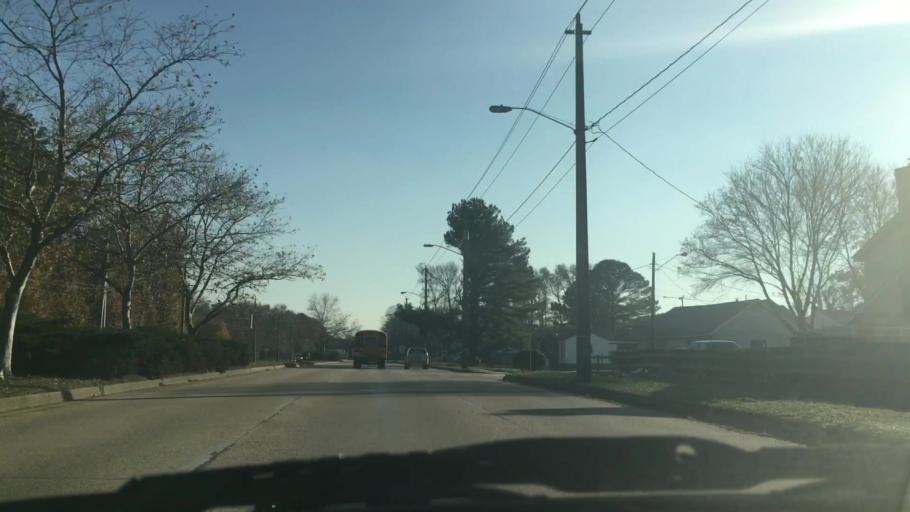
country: US
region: Virginia
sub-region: City of Norfolk
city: Norfolk
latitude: 36.9067
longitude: -76.2402
